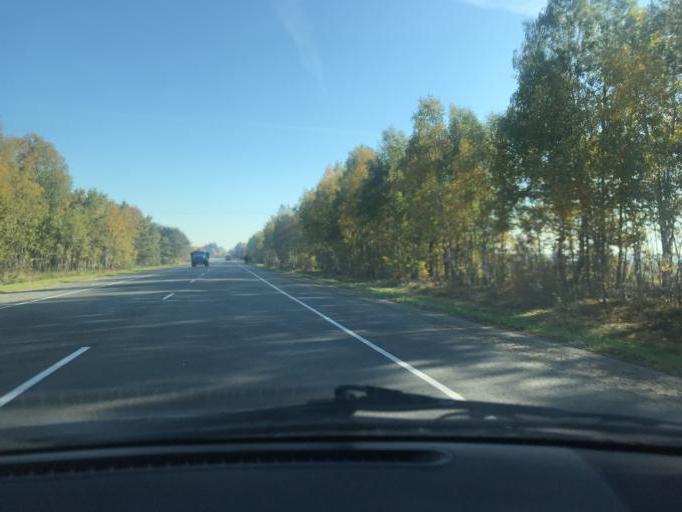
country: BY
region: Brest
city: Ivanava
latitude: 52.1542
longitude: 25.6104
